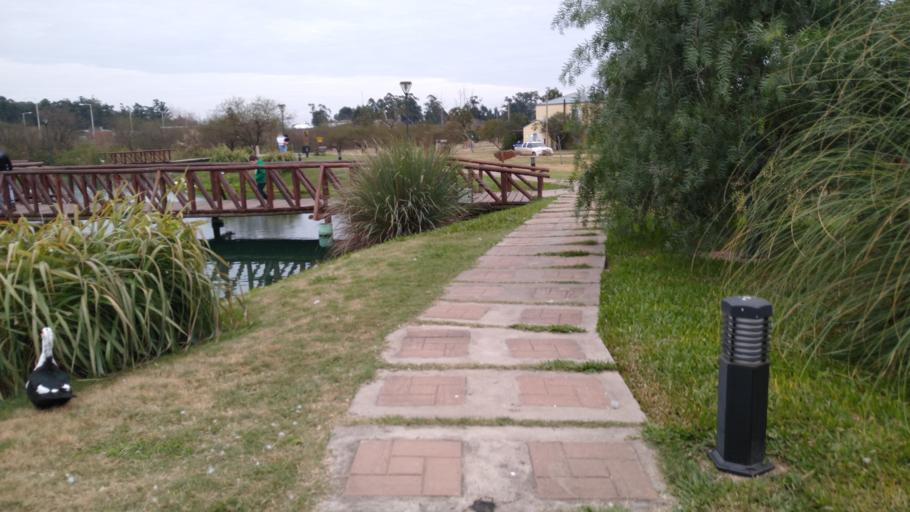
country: AR
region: Entre Rios
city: Chajari
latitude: -30.7433
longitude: -58.0147
